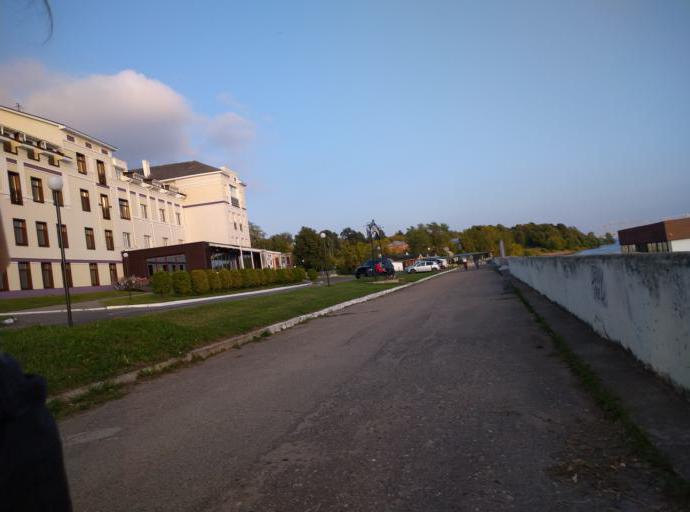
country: RU
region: Kostroma
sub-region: Kostromskoy Rayon
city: Kostroma
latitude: 57.7506
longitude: 40.9511
